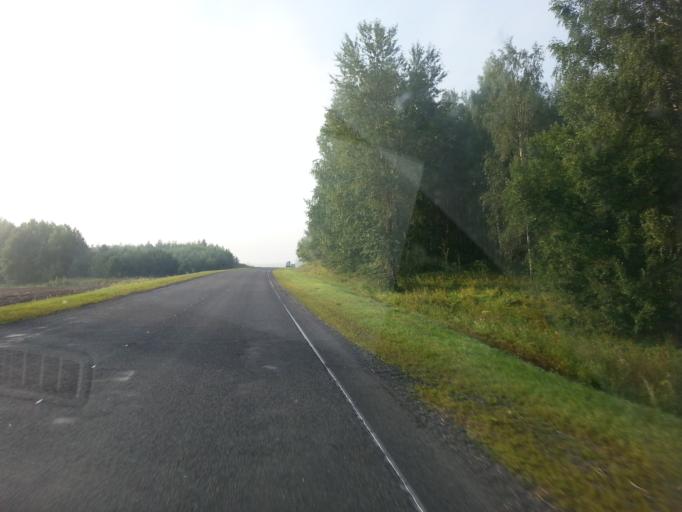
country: BY
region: Minsk
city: Kryvichy
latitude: 54.7371
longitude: 27.1335
